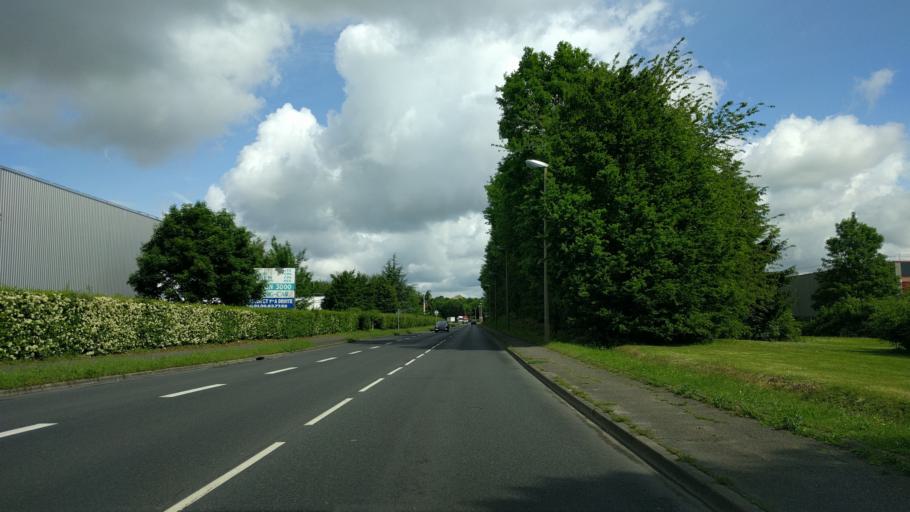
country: FR
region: Ile-de-France
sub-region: Departement de Seine-et-Marne
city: Savigny-le-Temple
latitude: 48.5905
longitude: 2.5920
